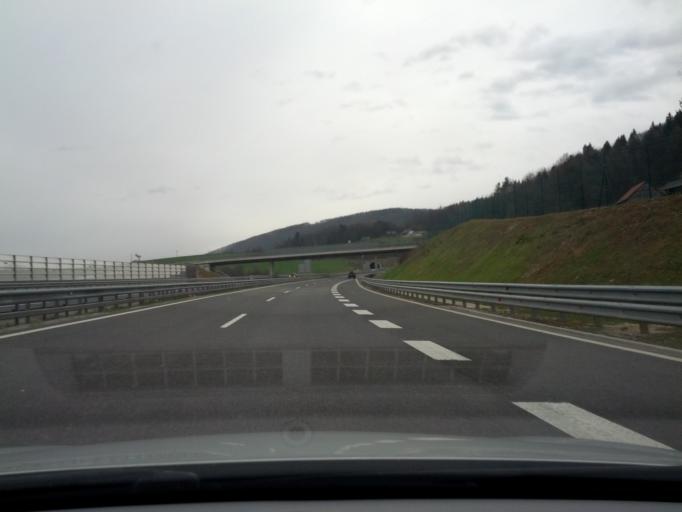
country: SI
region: Trebnje
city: Trebnje
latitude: 45.9094
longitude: 14.9692
